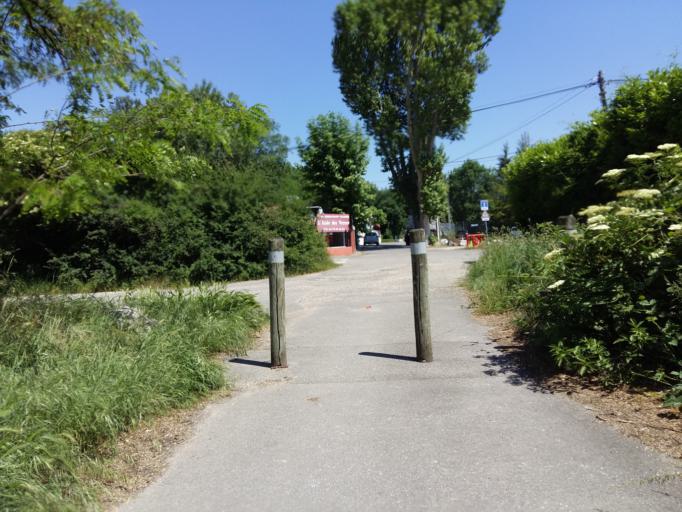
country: FR
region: Rhone-Alpes
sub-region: Departement du Rhone
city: Decines-Charpieu
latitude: 45.7950
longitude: 4.9695
